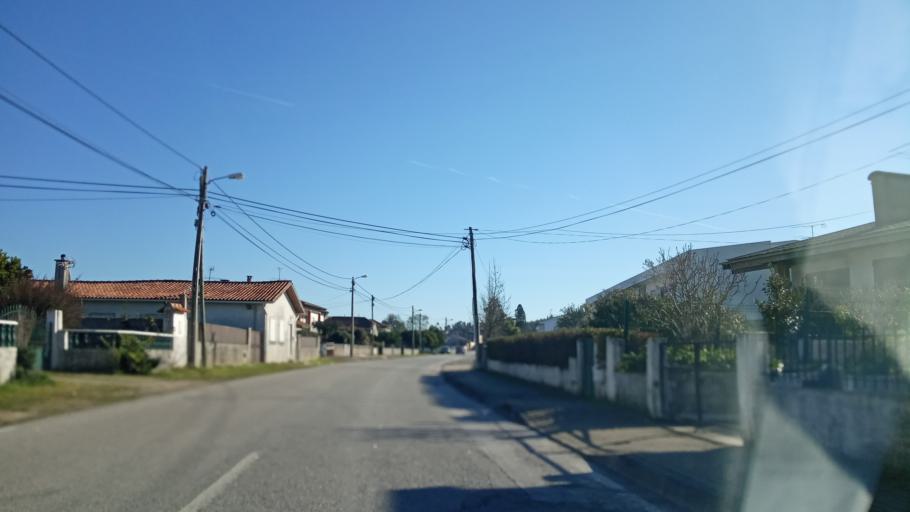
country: PT
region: Aveiro
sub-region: Anadia
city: Anadia
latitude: 40.4305
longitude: -8.4297
